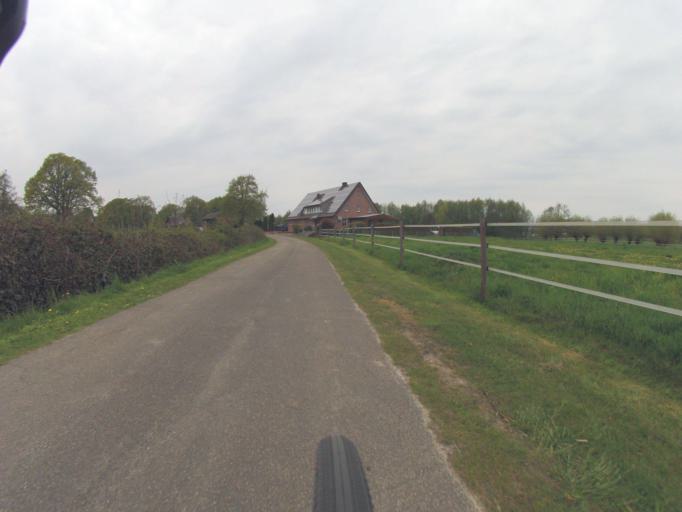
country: DE
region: North Rhine-Westphalia
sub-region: Regierungsbezirk Munster
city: Mettingen
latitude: 52.3104
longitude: 7.8081
